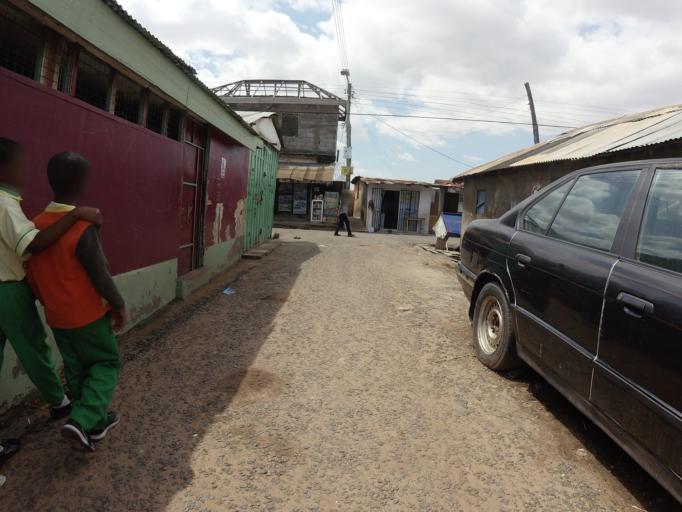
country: GH
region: Greater Accra
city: Accra
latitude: 5.5833
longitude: -0.1992
